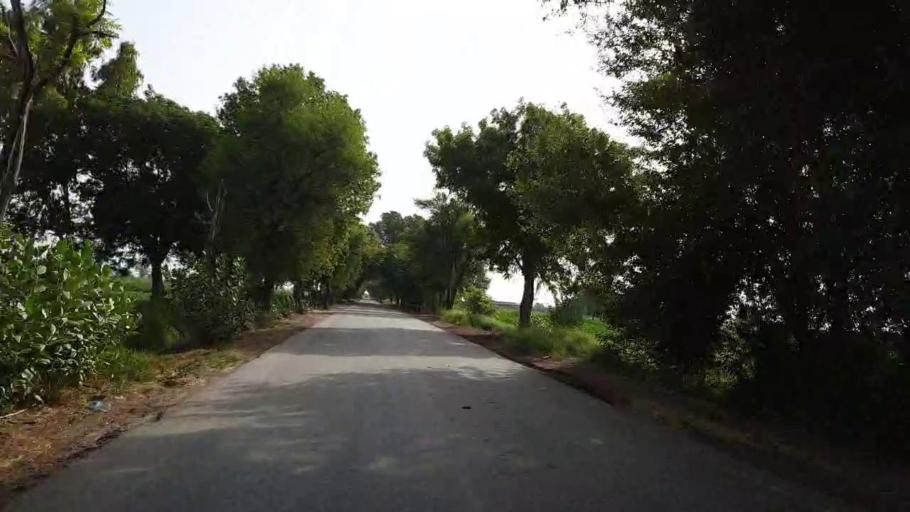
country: PK
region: Sindh
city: Nawabshah
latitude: 26.2503
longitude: 68.4611
